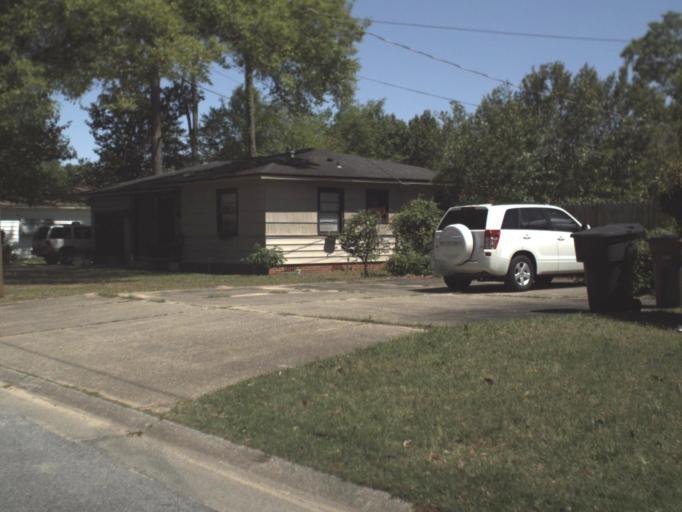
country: US
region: Florida
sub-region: Escambia County
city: Goulding
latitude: 30.4475
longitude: -87.2124
